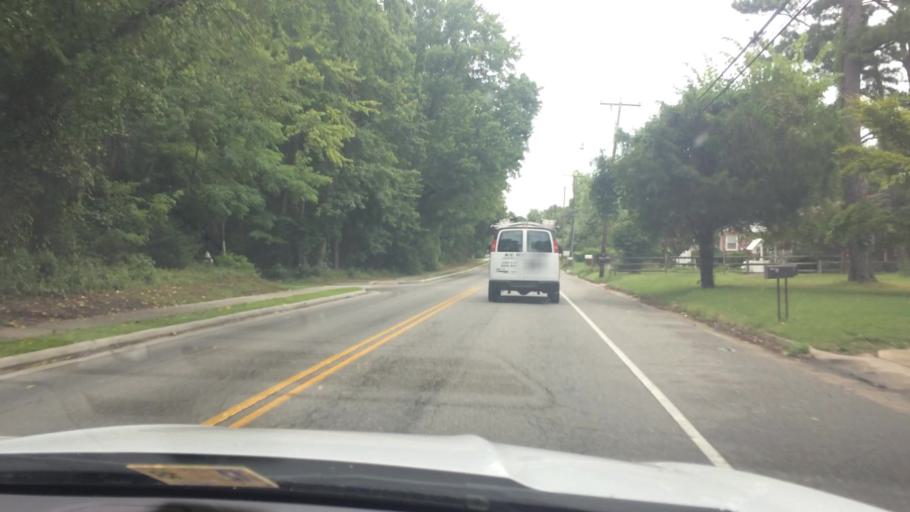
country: US
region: Virginia
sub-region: City of Williamsburg
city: Williamsburg
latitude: 37.2693
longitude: -76.6721
